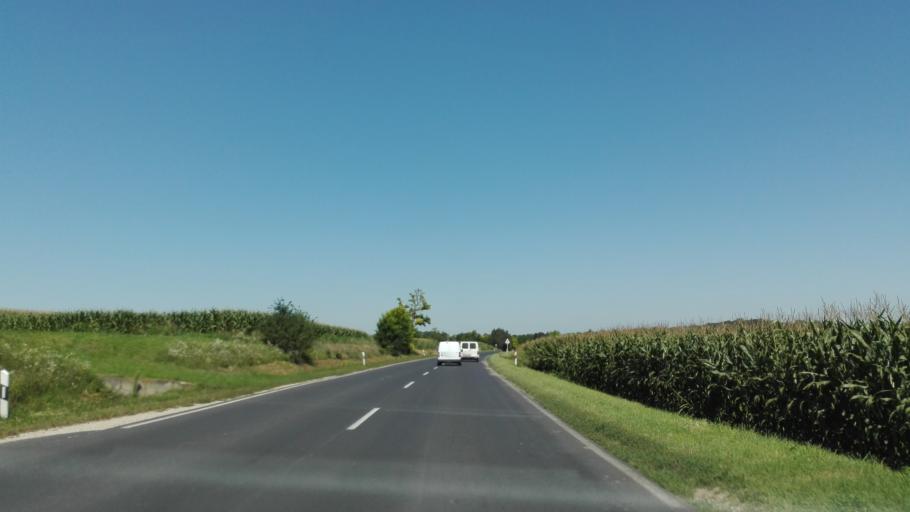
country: HU
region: Fejer
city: Mezoszilas
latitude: 46.7971
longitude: 18.4918
